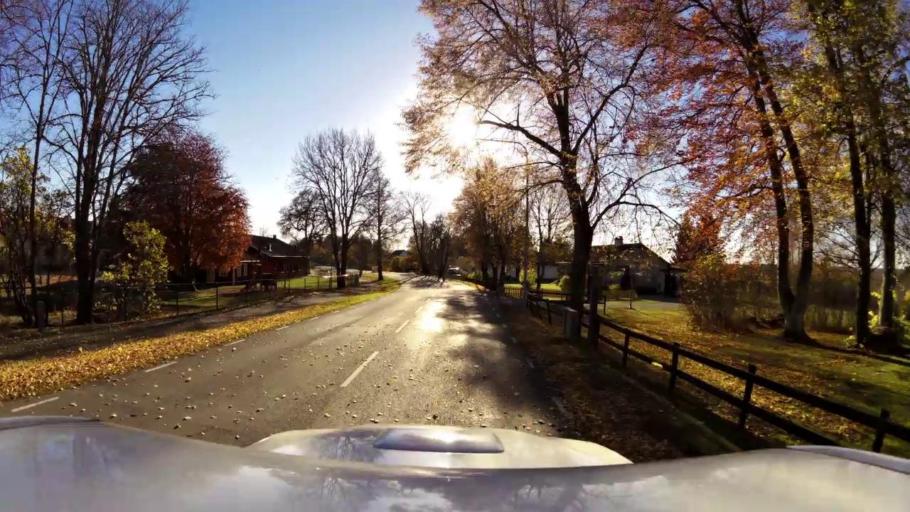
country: SE
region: OEstergoetland
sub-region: Linkopings Kommun
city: Malmslatt
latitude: 58.3706
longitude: 15.5567
